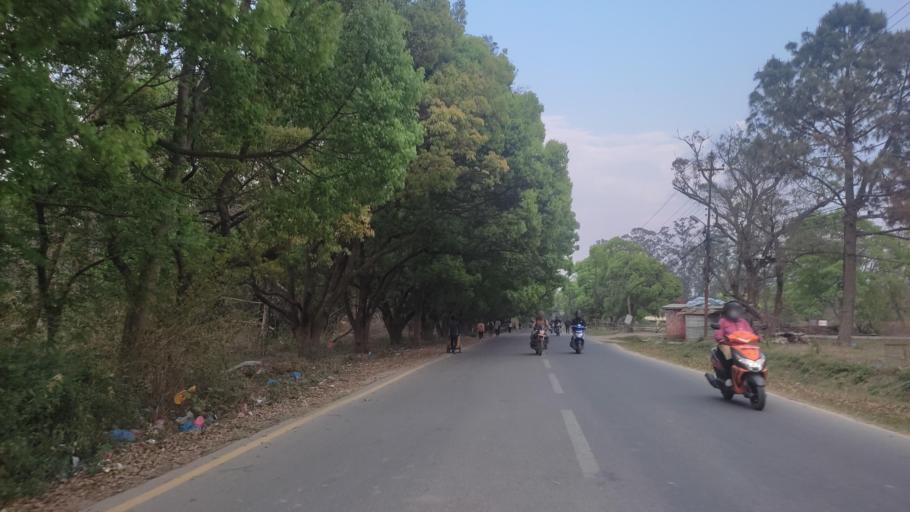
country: NP
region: Central Region
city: Kirtipur
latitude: 27.6786
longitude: 85.2860
